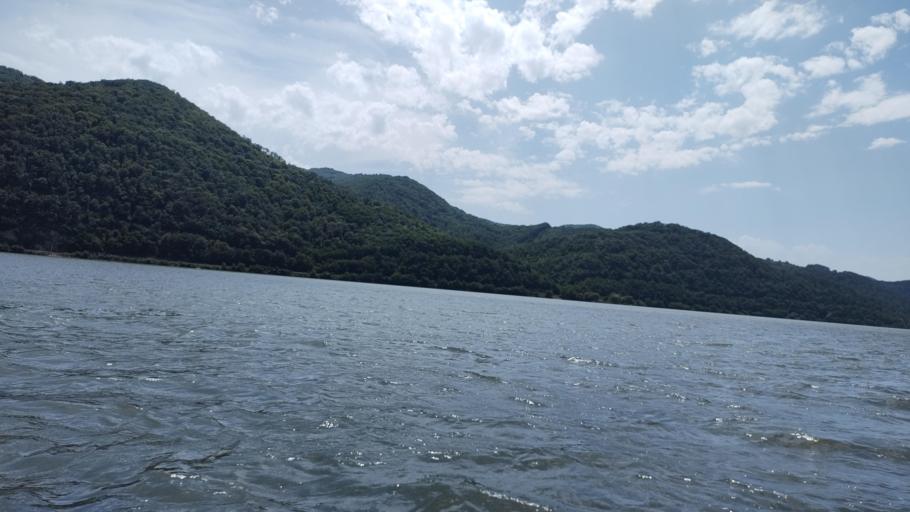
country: RO
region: Caras-Severin
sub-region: Comuna Berzasca
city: Liubcova
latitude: 44.6487
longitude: 21.8895
